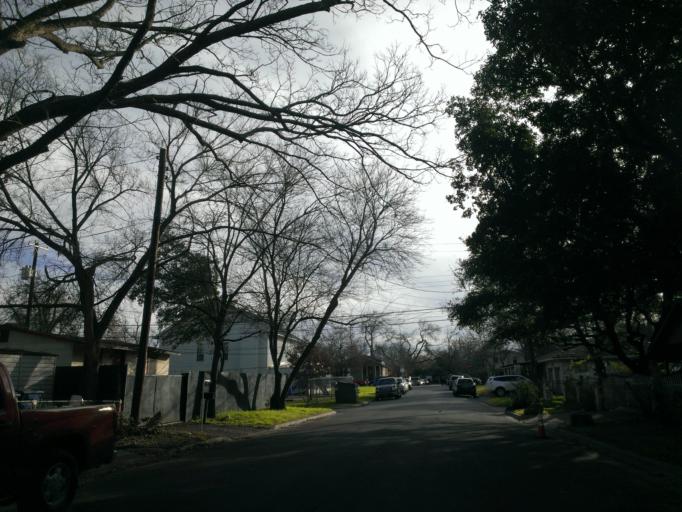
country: US
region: Texas
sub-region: Travis County
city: Austin
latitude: 30.2585
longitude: -97.7229
